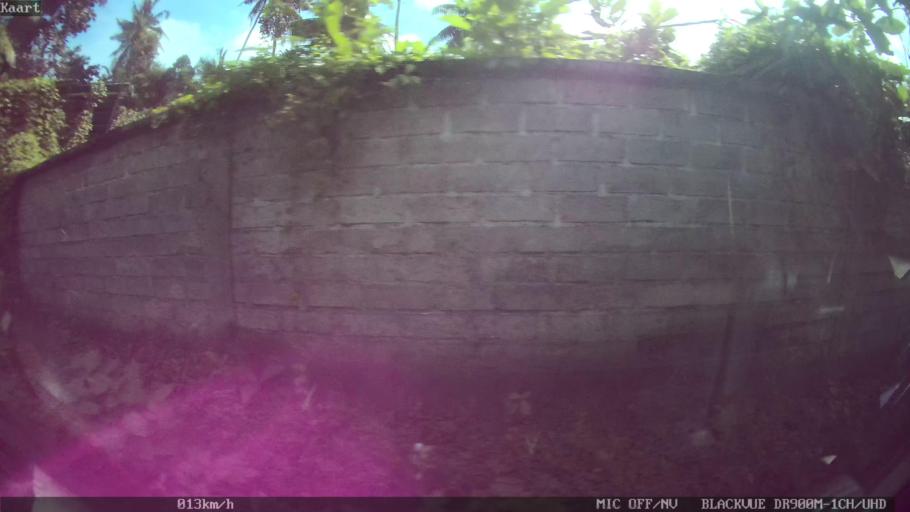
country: ID
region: Bali
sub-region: Kabupaten Gianyar
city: Ubud
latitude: -8.5095
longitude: 115.2737
